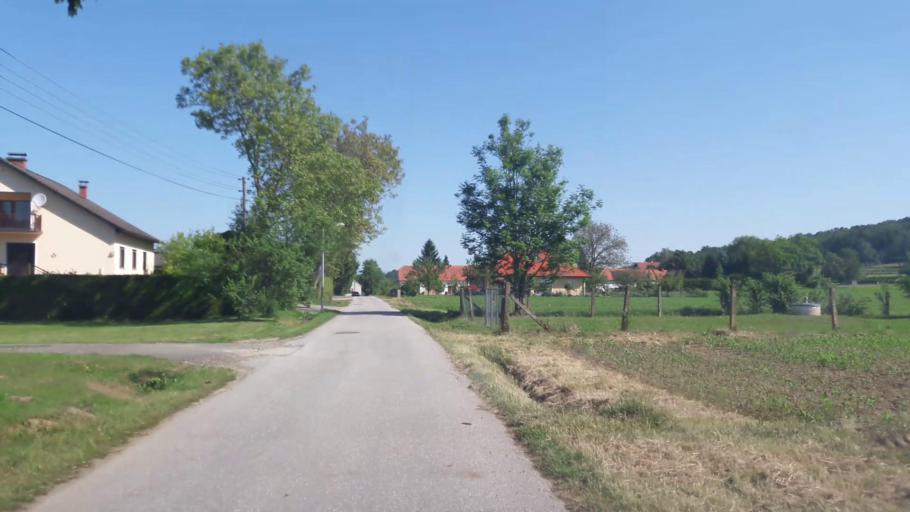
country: AT
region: Burgenland
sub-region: Politischer Bezirk Jennersdorf
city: Deutsch Kaltenbrunn
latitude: 47.0892
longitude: 16.1092
